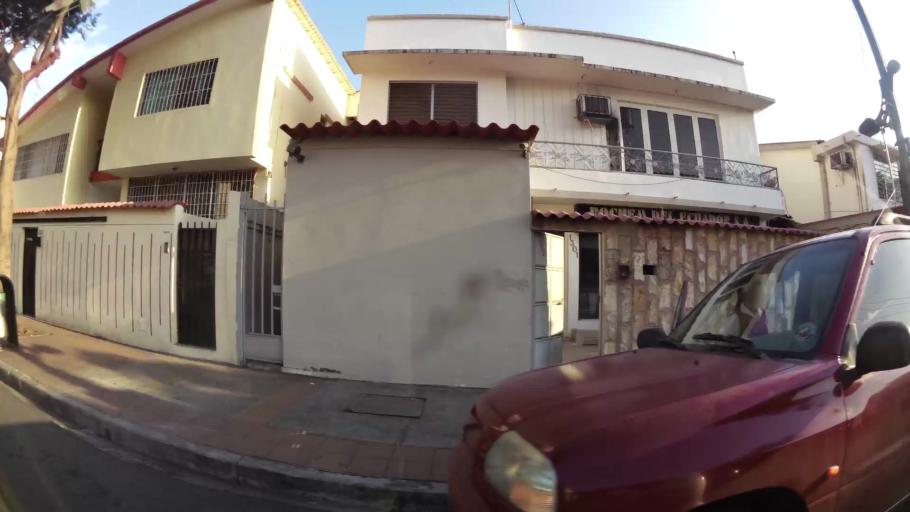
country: EC
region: Guayas
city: Guayaquil
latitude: -2.2140
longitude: -79.8940
